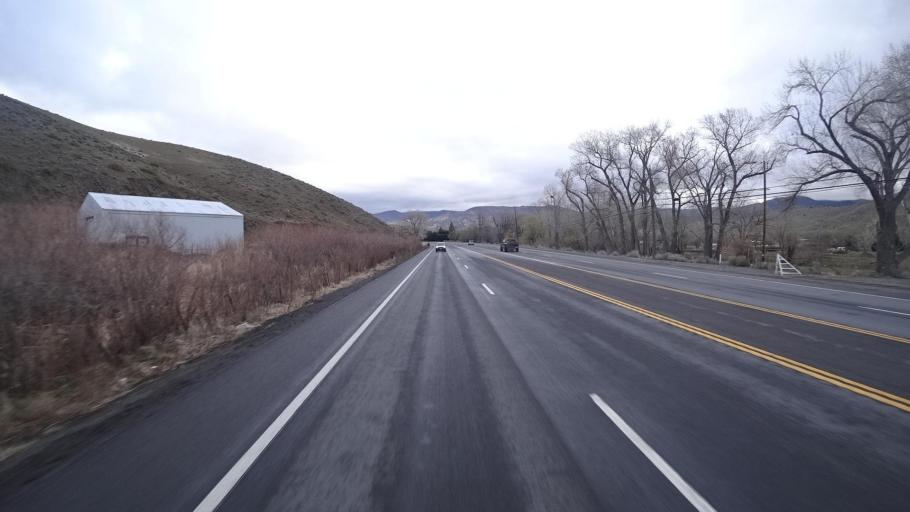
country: US
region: Nevada
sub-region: Storey County
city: Virginia City
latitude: 39.3639
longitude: -119.7552
